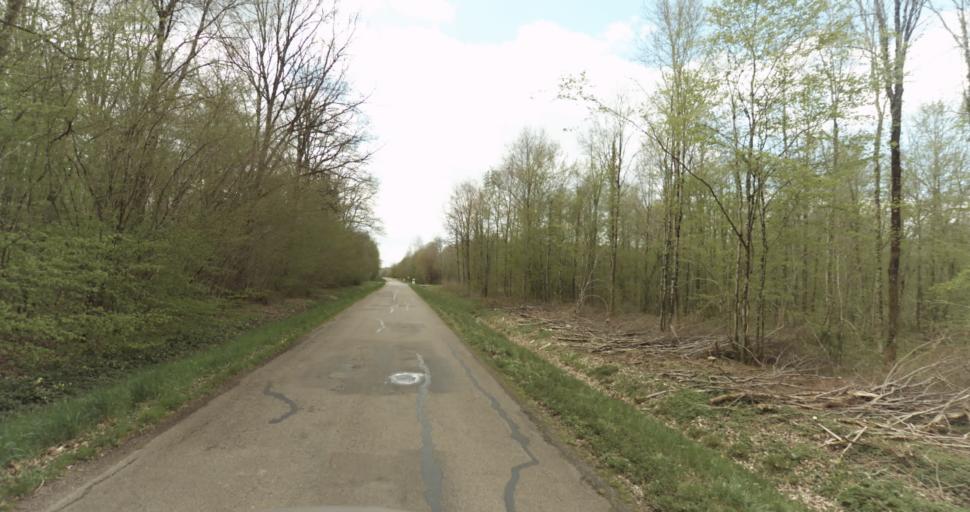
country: FR
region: Bourgogne
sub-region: Departement de la Cote-d'Or
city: Auxonne
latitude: 47.1828
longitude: 5.4487
